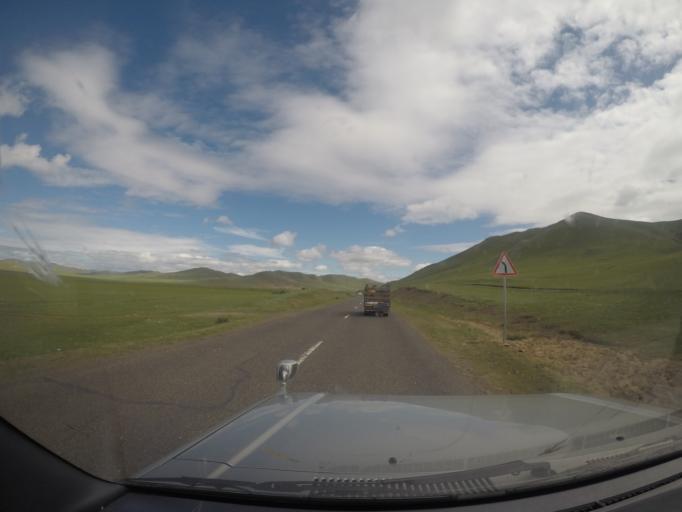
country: MN
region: Hentiy
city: Modot
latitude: 47.6834
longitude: 109.1025
